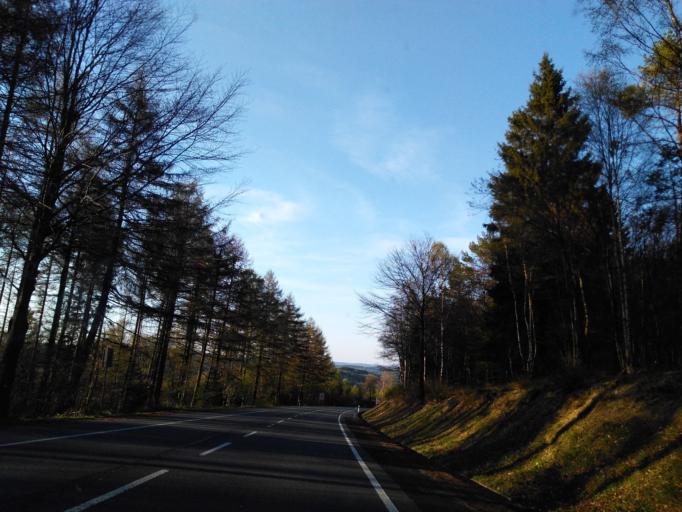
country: DE
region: North Rhine-Westphalia
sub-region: Regierungsbezirk Arnsberg
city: Herscheid
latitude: 51.1464
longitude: 7.7455
